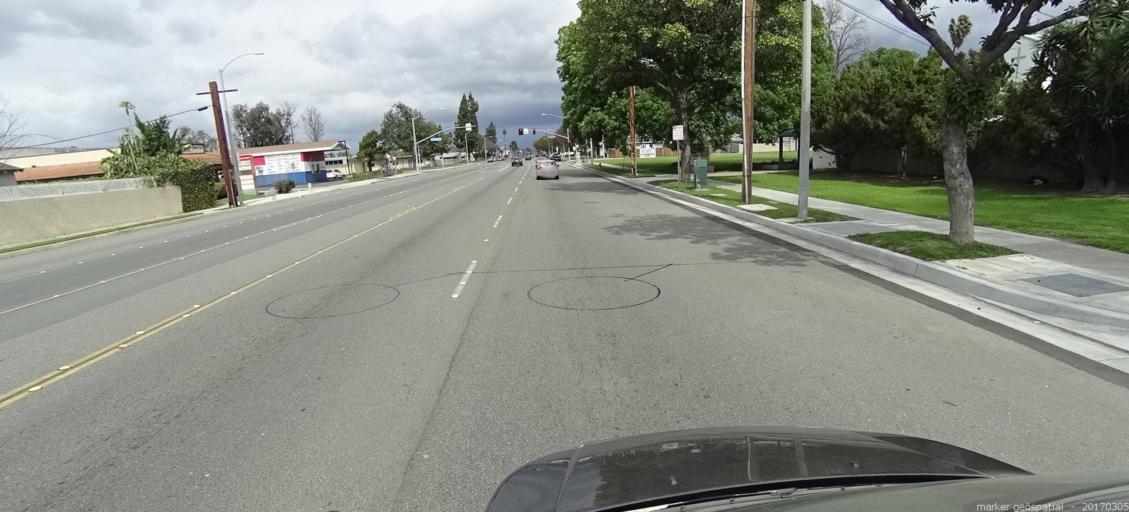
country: US
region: California
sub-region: Orange County
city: Stanton
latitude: 33.8238
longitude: -117.9759
